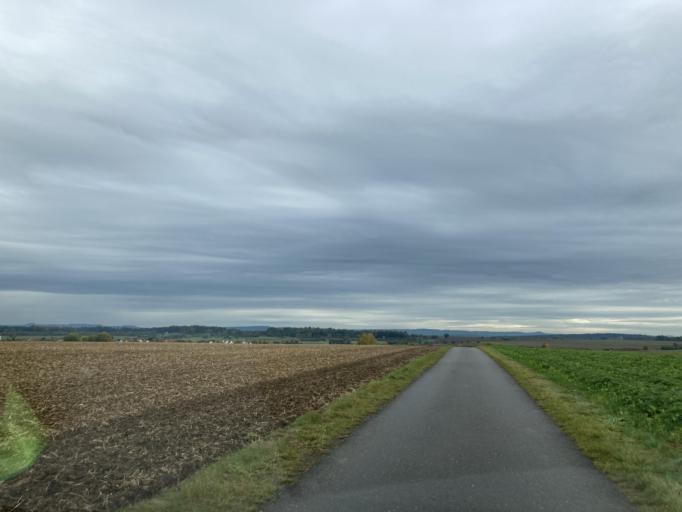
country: DE
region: Baden-Wuerttemberg
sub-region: Regierungsbezirk Stuttgart
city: Bondorf
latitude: 48.5345
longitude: 8.8526
